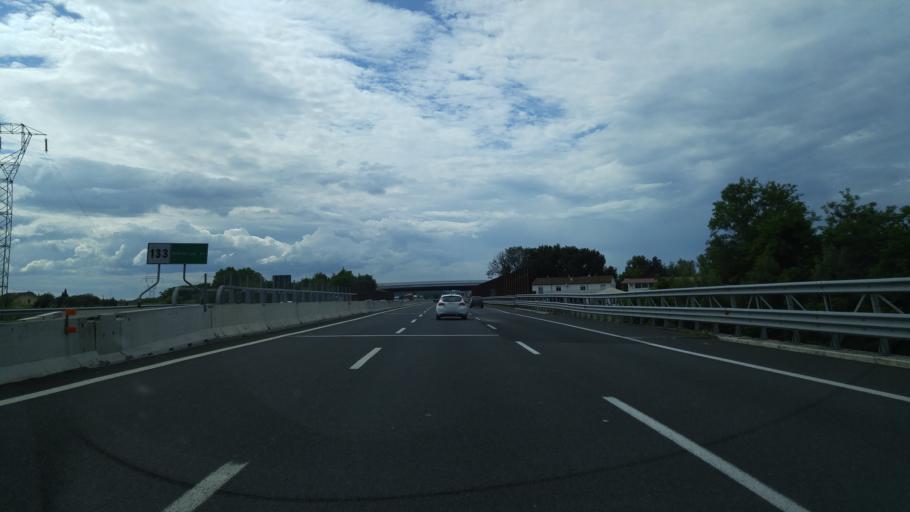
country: IT
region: Emilia-Romagna
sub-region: Provincia di Rimini
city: Coriano
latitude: 43.9973
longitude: 12.6139
